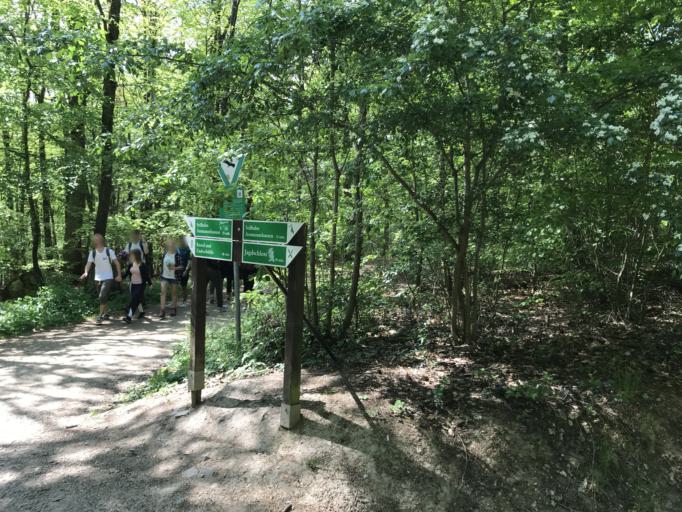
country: DE
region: Rheinland-Pfalz
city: Bingen am Rhein
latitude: 49.9796
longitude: 7.8829
